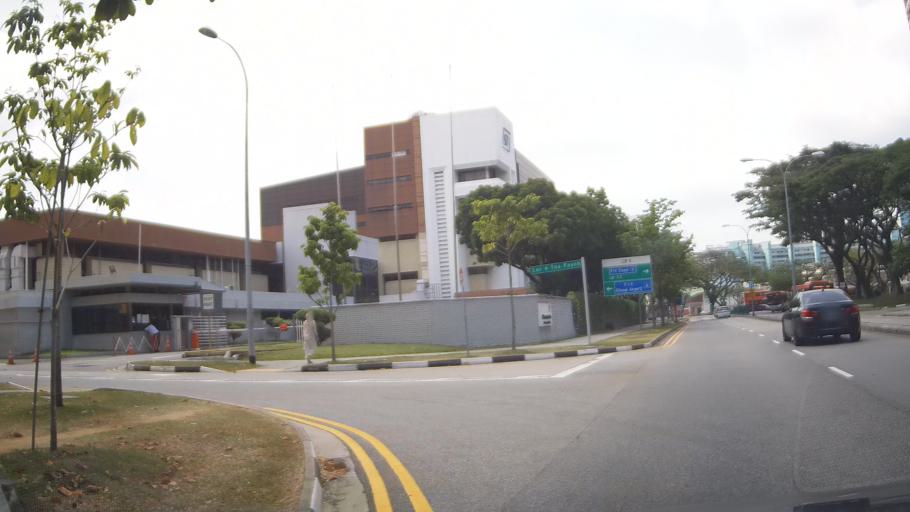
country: SG
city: Singapore
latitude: 1.3329
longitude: 103.8516
